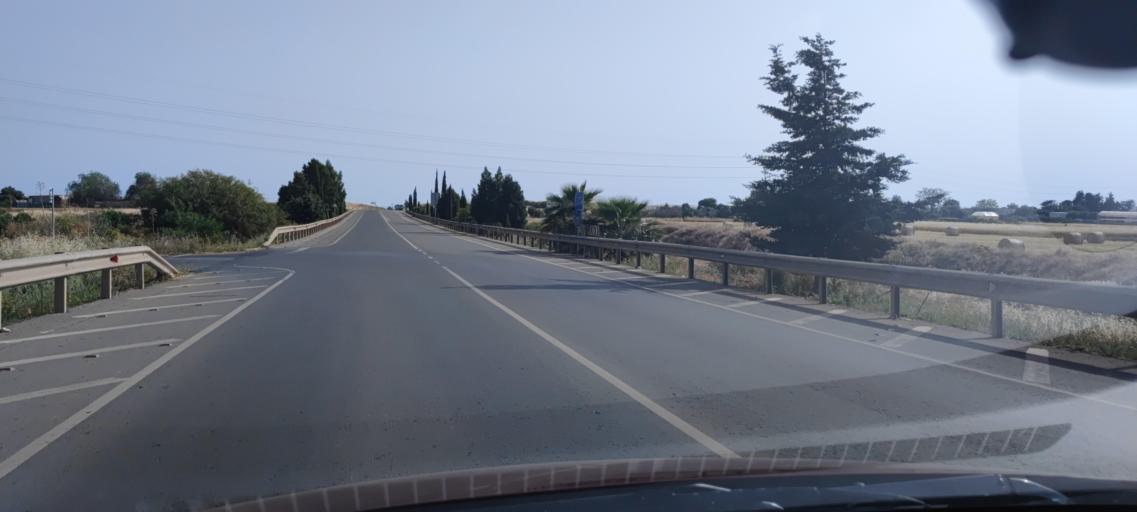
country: CY
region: Ammochostos
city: Frenaros
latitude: 35.0049
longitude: 33.9371
